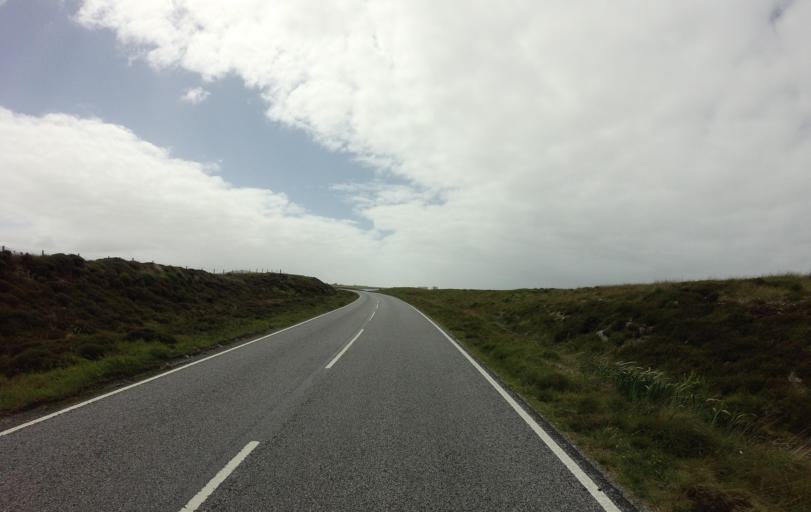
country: GB
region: Scotland
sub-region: Eilean Siar
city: Benbecula
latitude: 57.3643
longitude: -7.3538
